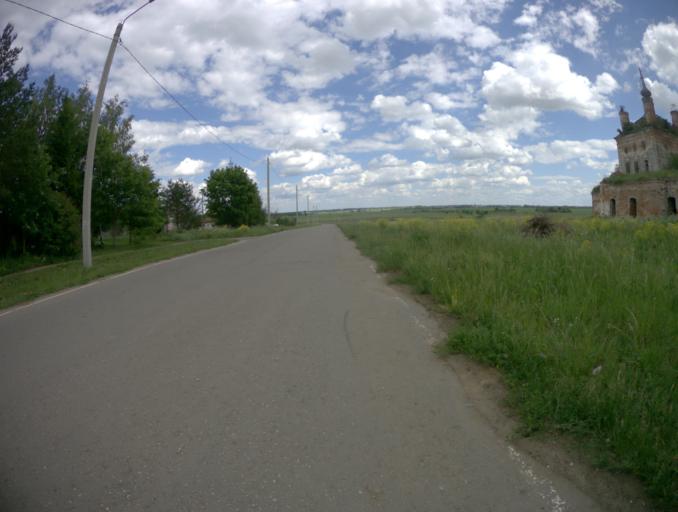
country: RU
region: Vladimir
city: Suzdal'
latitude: 56.4409
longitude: 40.3877
